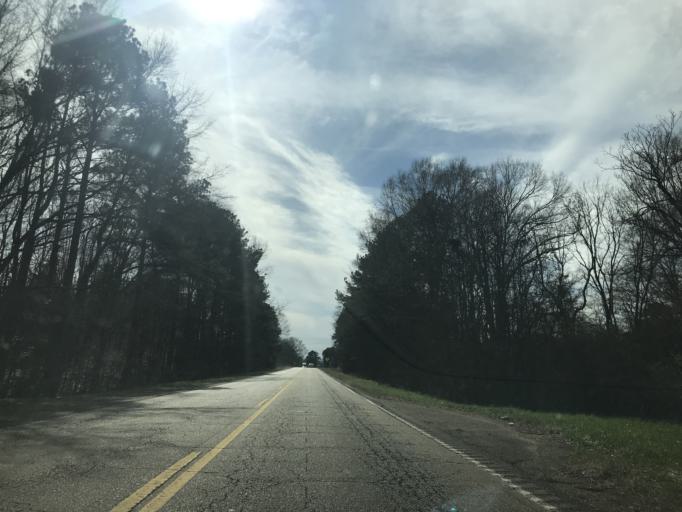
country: US
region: Mississippi
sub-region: Hinds County
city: Edwards
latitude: 32.1072
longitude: -90.6116
